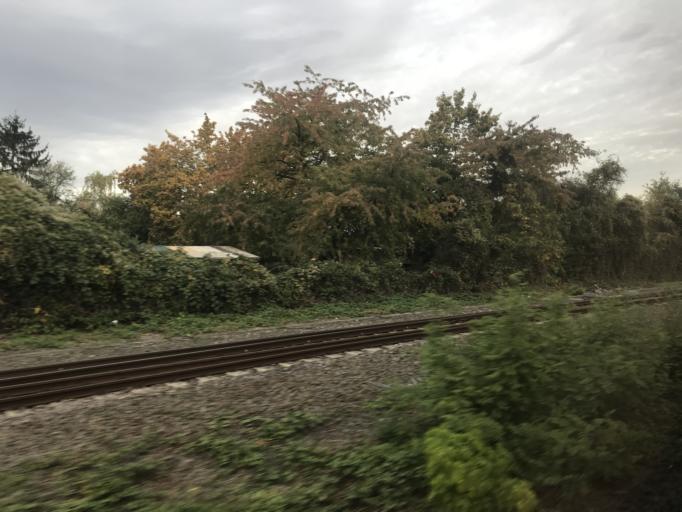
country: DE
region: Rheinland-Pfalz
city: Alzey
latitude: 49.7526
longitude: 8.1121
